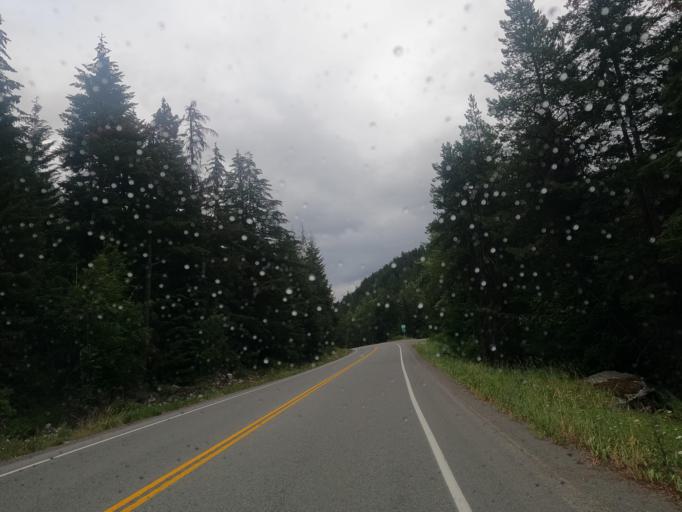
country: CA
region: British Columbia
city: Lillooet
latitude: 50.5284
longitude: -122.1591
